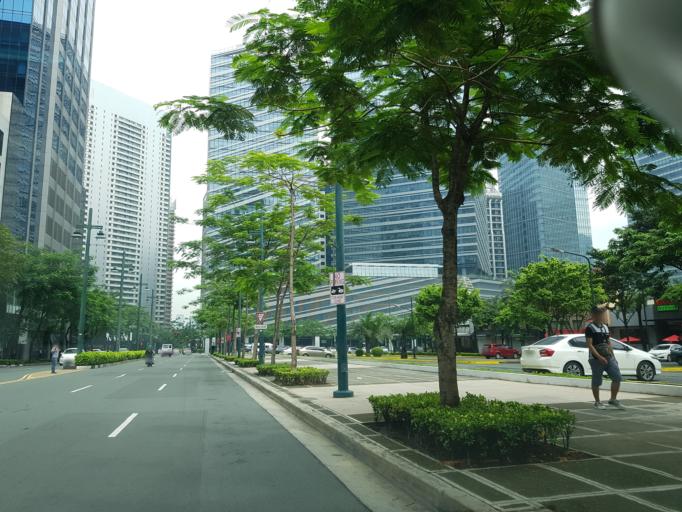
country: PH
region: Metro Manila
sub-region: Makati City
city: Makati City
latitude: 14.5485
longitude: 121.0485
